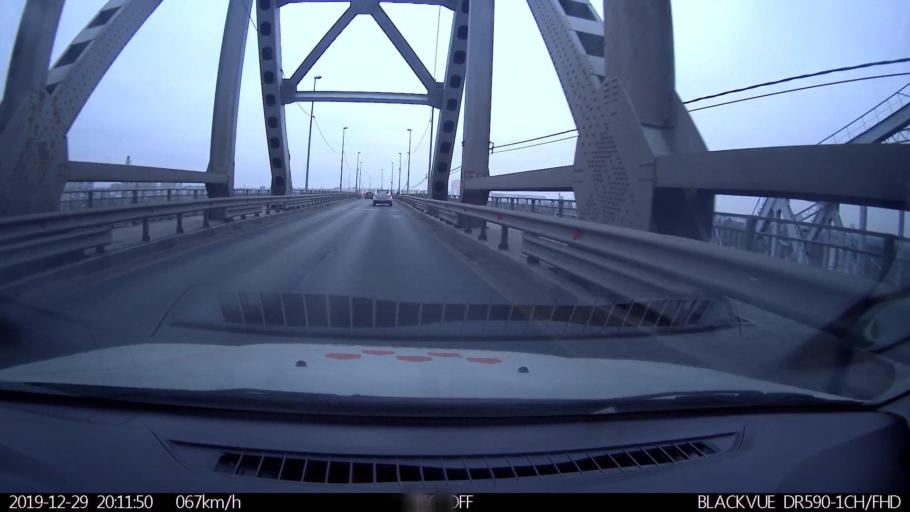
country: RU
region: Nizjnij Novgorod
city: Nizhniy Novgorod
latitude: 56.3519
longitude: 43.9234
